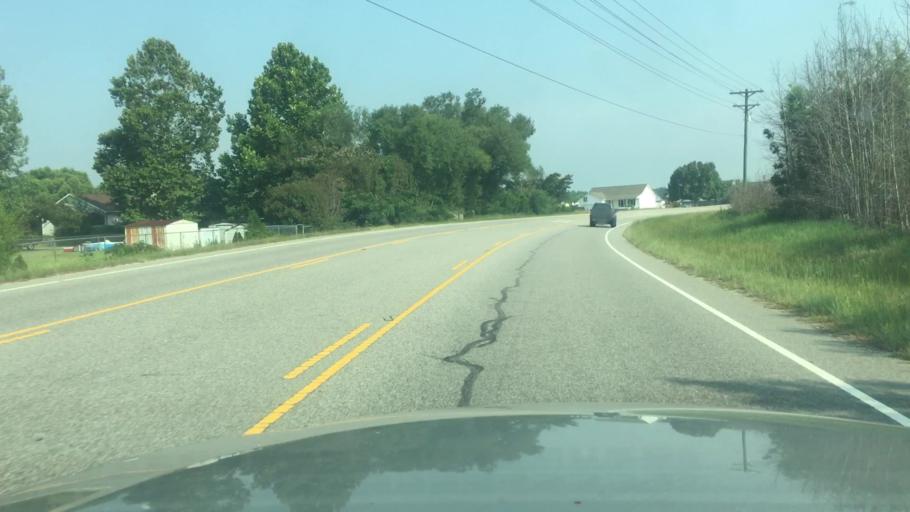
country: US
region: North Carolina
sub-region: Cumberland County
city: Hope Mills
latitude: 34.9178
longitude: -78.9100
